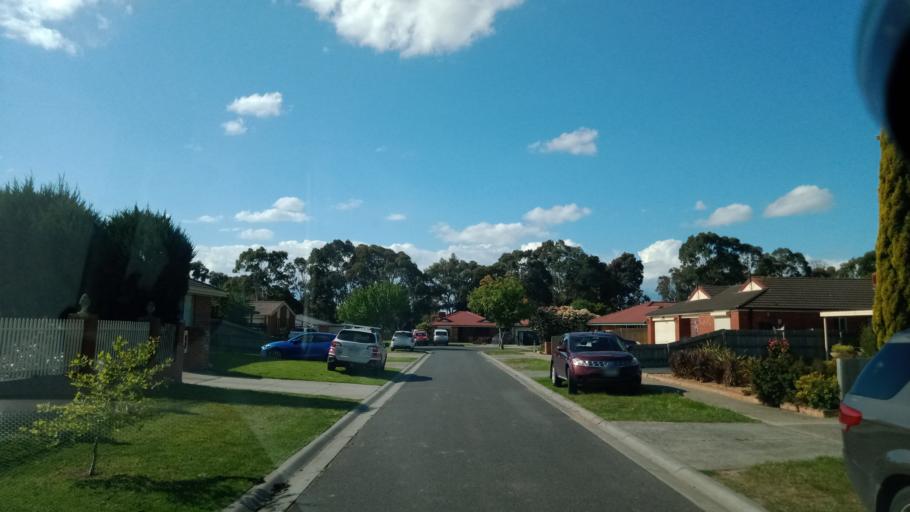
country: AU
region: Victoria
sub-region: Casey
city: Cranbourne West
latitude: -38.0972
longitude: 145.2664
